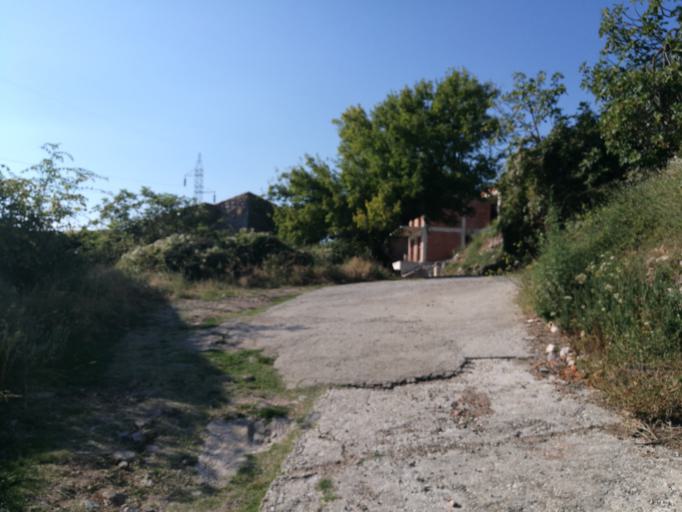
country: ME
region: Budva
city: Budva
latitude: 42.2814
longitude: 18.8923
